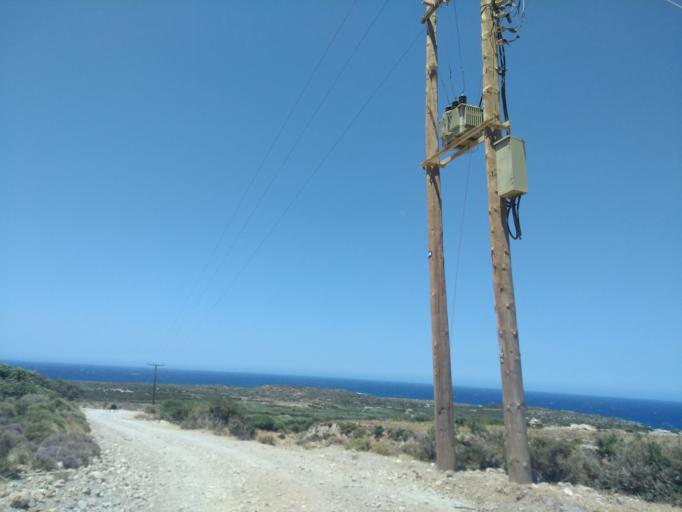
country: GR
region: Crete
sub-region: Nomos Chanias
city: Palaiochora
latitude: 35.3036
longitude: 23.5444
